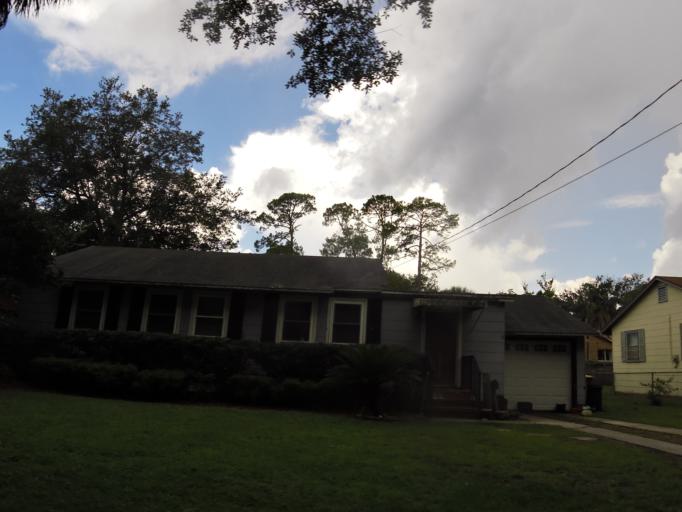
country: US
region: Florida
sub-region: Duval County
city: Jacksonville
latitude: 30.2968
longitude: -81.6333
